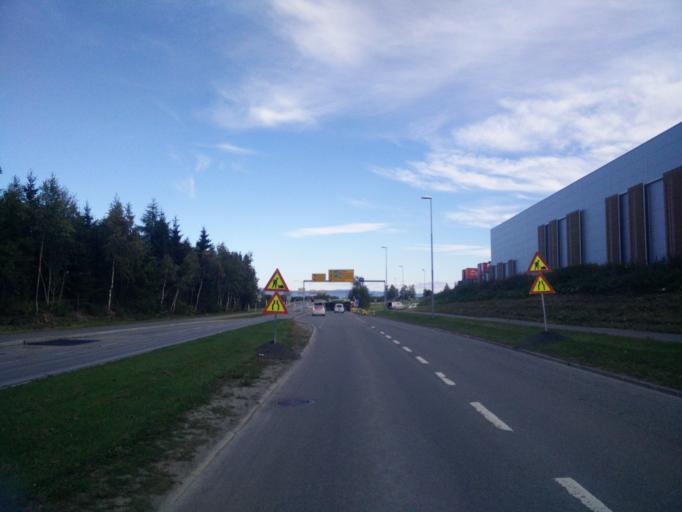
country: NO
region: Sor-Trondelag
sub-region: Trondheim
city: Trondheim
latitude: 63.3690
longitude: 10.3766
